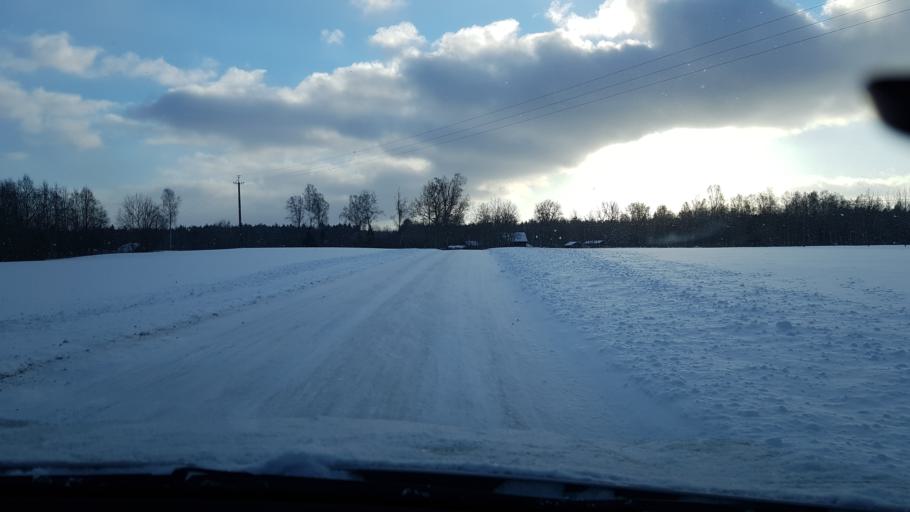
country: EE
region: Harju
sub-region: Nissi vald
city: Turba
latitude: 59.1646
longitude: 24.1424
